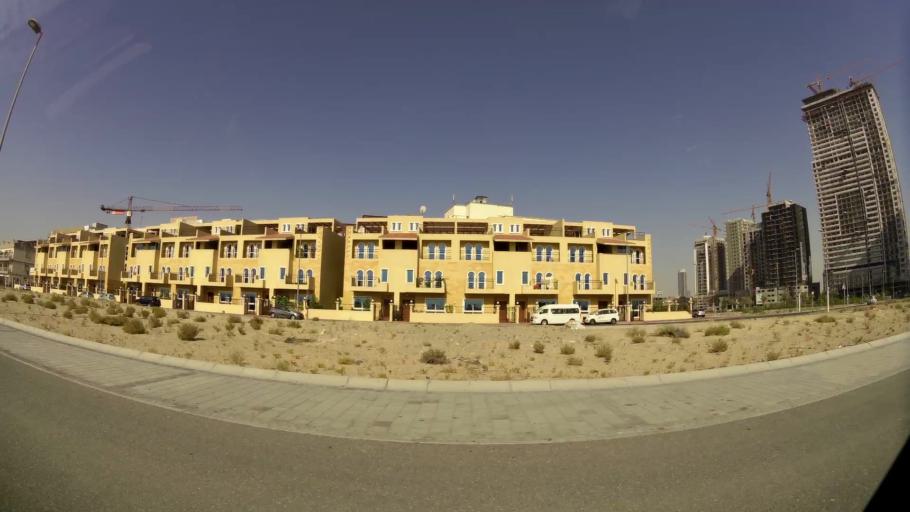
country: AE
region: Dubai
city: Dubai
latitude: 25.0555
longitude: 55.1974
